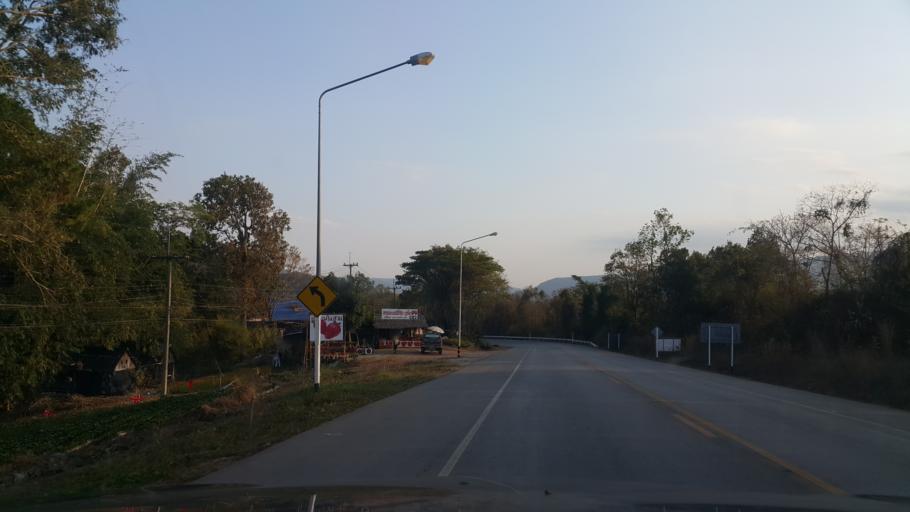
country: TH
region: Loei
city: Phu Ruea
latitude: 17.4546
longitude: 101.4998
